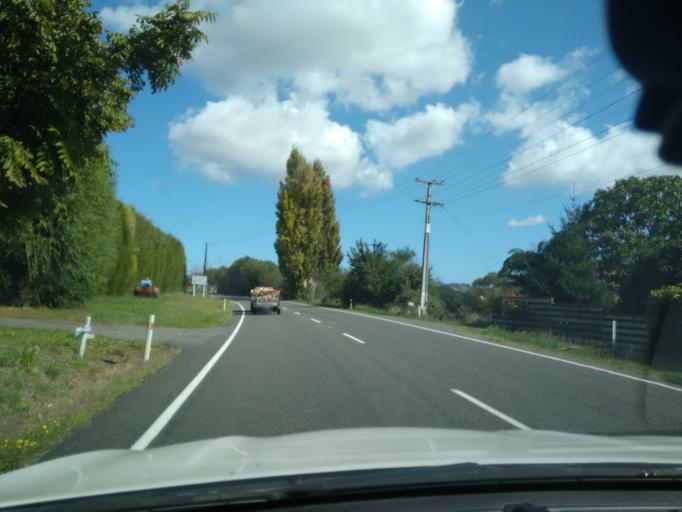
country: NZ
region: Manawatu-Wanganui
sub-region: Wanganui District
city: Wanganui
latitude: -39.9005
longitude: 175.0716
